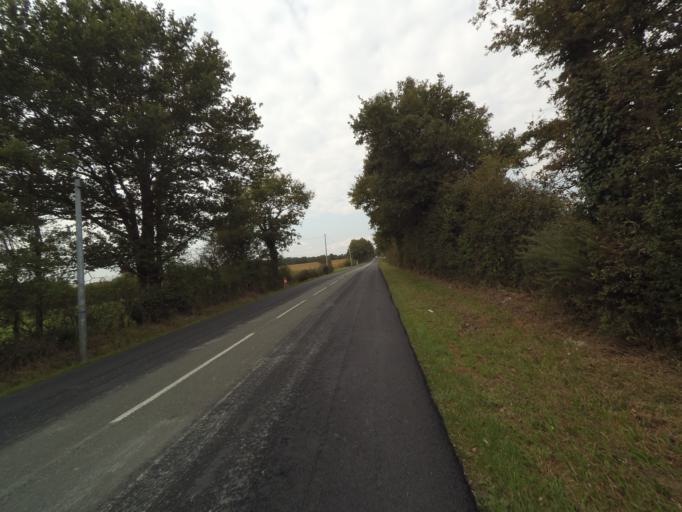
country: FR
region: Pays de la Loire
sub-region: Departement de la Vendee
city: Bouffere
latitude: 46.9859
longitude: -1.3570
